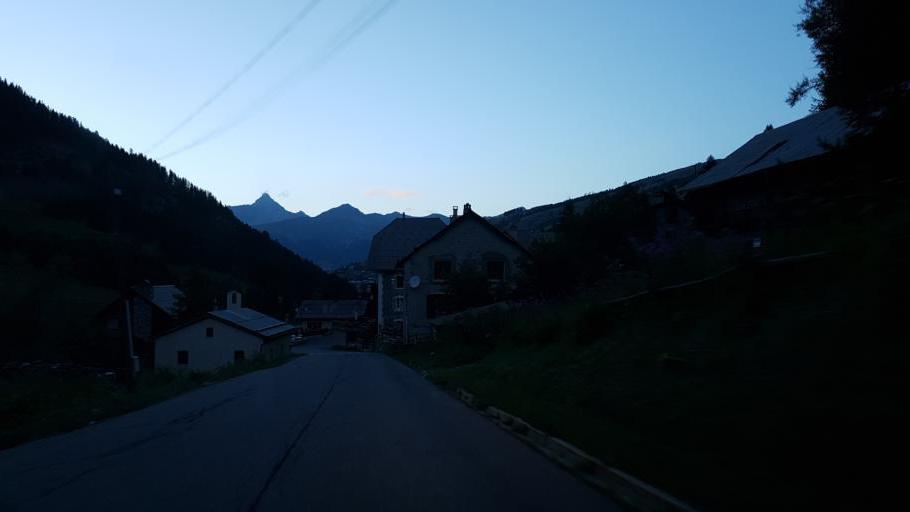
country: IT
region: Piedmont
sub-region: Provincia di Cuneo
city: Pontechianale
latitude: 44.7102
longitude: 6.8497
